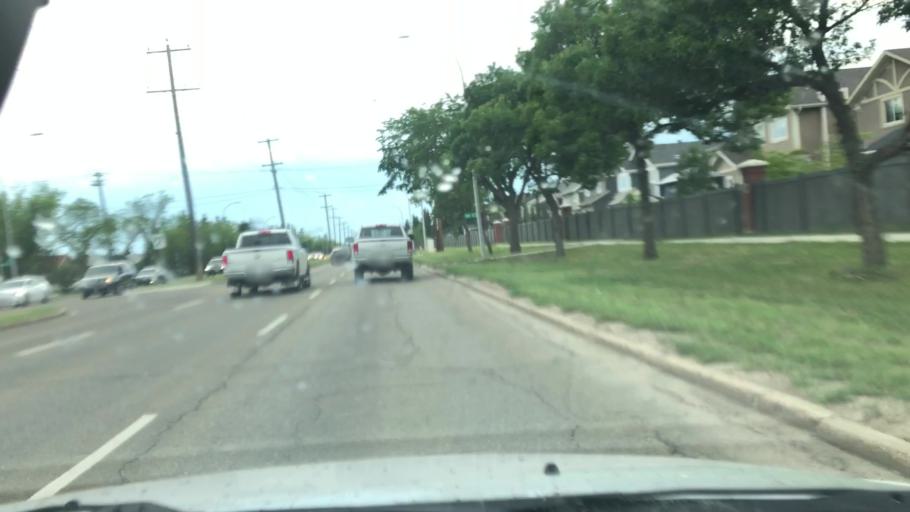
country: CA
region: Alberta
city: Edmonton
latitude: 53.5997
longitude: -113.5053
